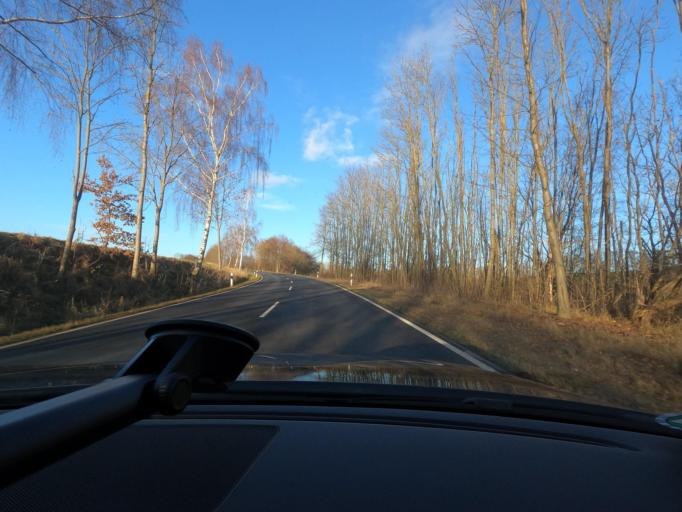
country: DE
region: Lower Saxony
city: Duderstadt
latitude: 51.5257
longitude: 10.2775
